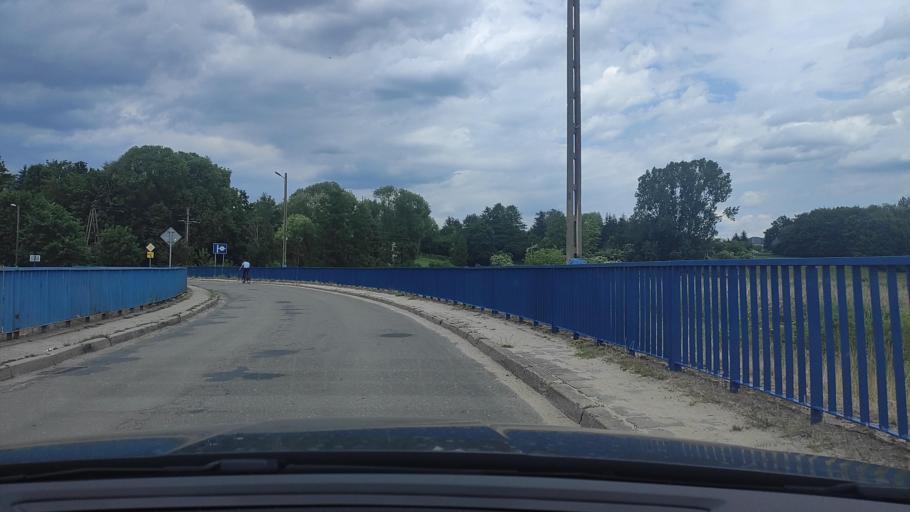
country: PL
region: Greater Poland Voivodeship
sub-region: Powiat poznanski
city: Kostrzyn
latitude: 52.4763
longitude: 17.1859
